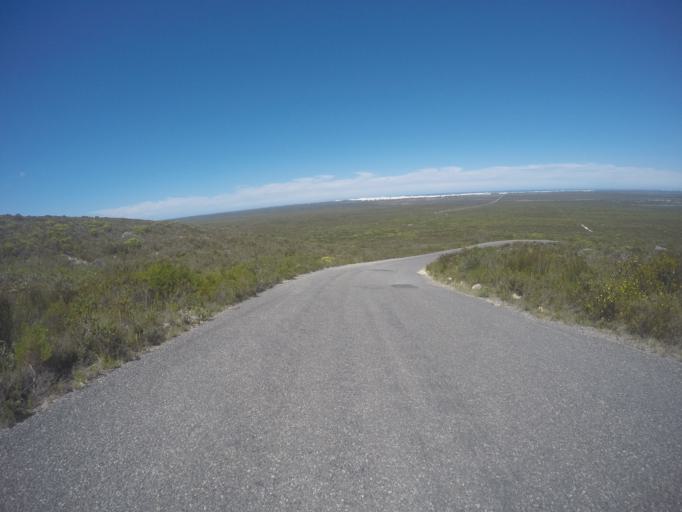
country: ZA
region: Western Cape
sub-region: Overberg District Municipality
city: Bredasdorp
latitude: -34.4264
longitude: 20.4146
